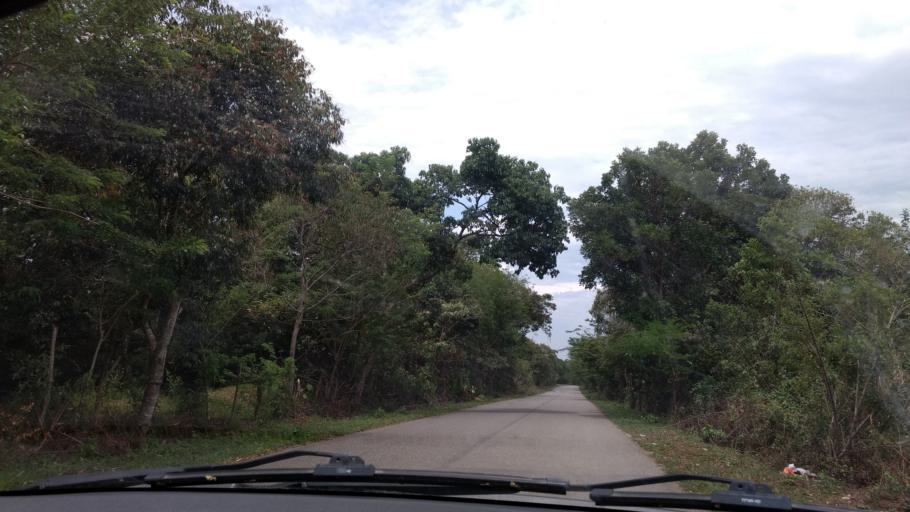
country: CO
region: Cauca
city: Buenos Aires
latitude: 3.0803
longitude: -76.6461
